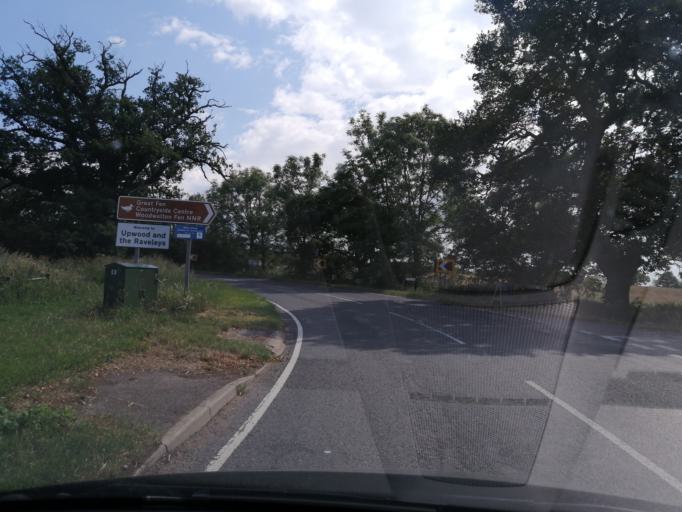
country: GB
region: England
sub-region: Cambridgeshire
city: Ramsey
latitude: 52.4465
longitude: -0.1599
